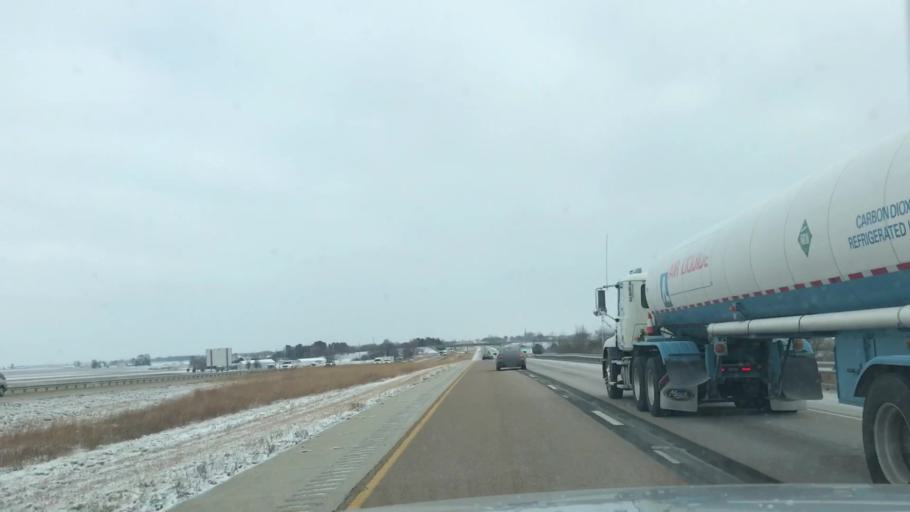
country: US
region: Illinois
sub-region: Montgomery County
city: Litchfield
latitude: 39.1987
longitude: -89.6641
